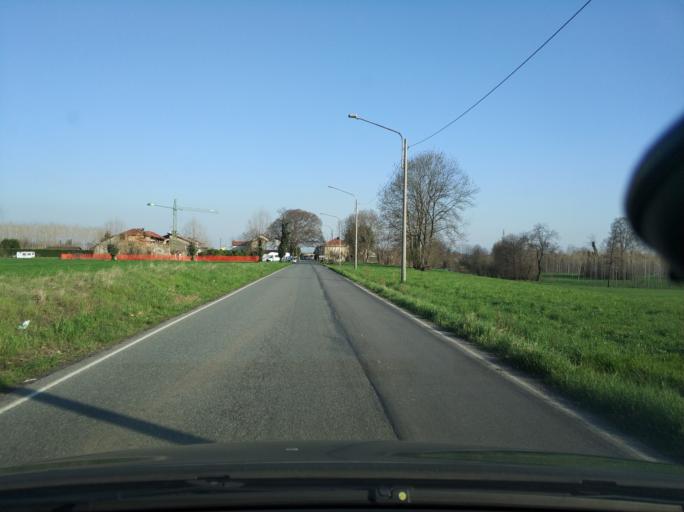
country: IT
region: Piedmont
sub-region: Provincia di Torino
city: Cirie
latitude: 45.2112
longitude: 7.5937
